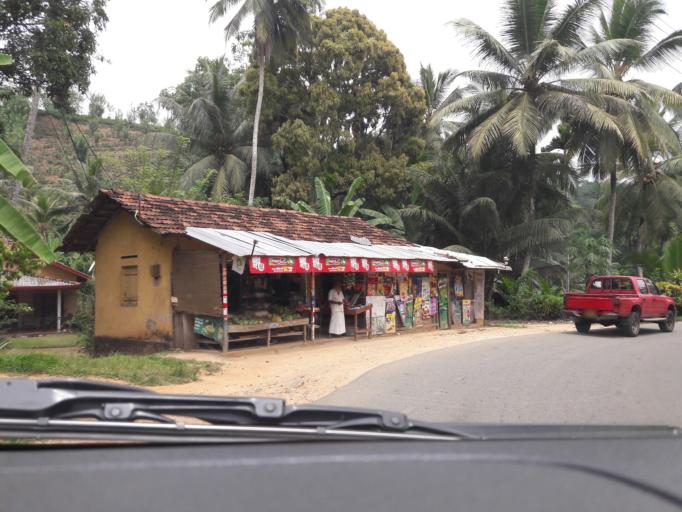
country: LK
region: Southern
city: Galle
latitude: 6.1830
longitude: 80.2951
